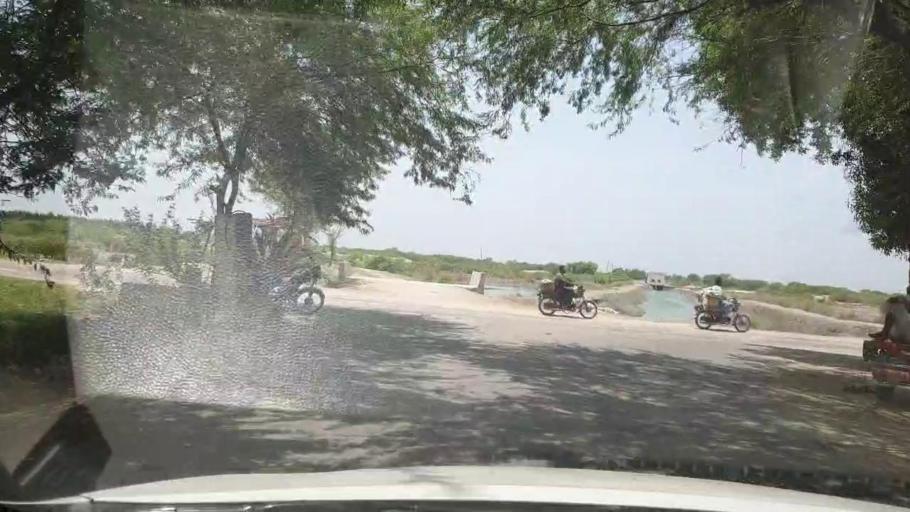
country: PK
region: Sindh
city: Bozdar
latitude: 27.2546
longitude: 68.6349
